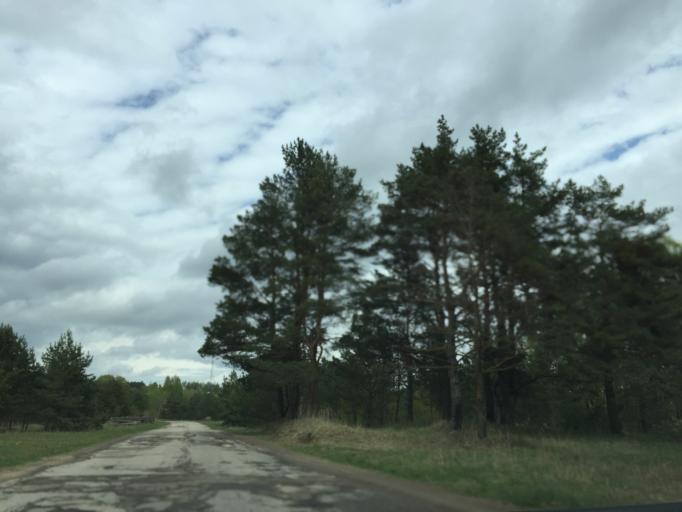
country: LV
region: Kekava
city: Kekava
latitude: 56.7886
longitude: 24.2997
